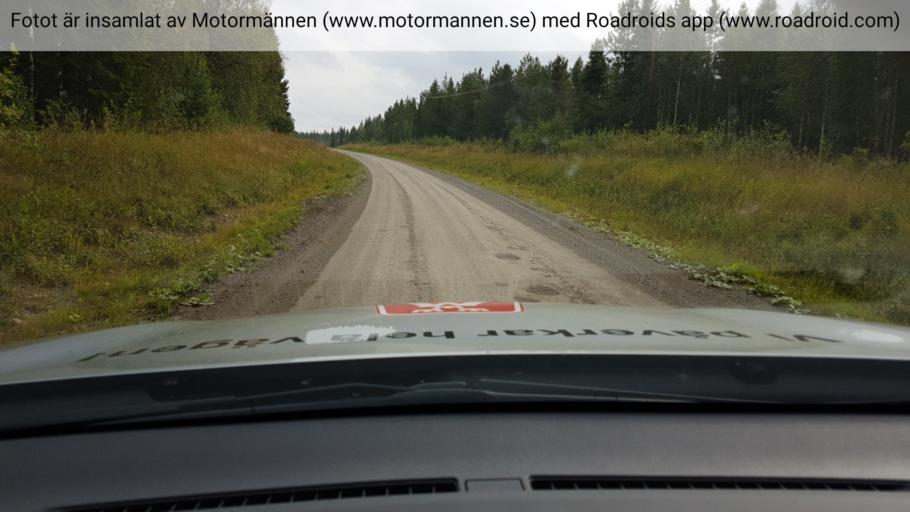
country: SE
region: Jaemtland
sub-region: Stroemsunds Kommun
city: Stroemsund
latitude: 63.7625
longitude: 15.3497
